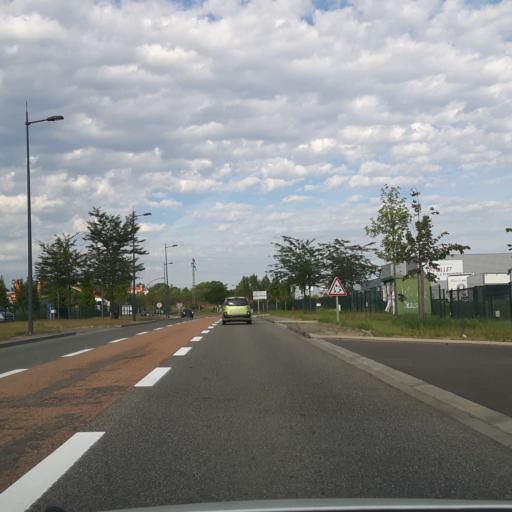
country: FR
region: Midi-Pyrenees
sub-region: Departement de la Haute-Garonne
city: Castelnau-d'Estretefonds
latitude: 43.7703
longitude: 1.3801
